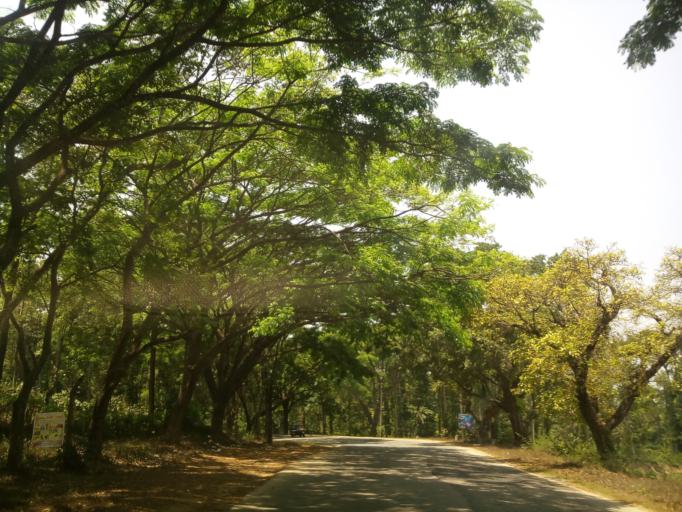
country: IN
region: Karnataka
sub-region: Hassan
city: Sakleshpur
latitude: 12.9521
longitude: 75.8208
